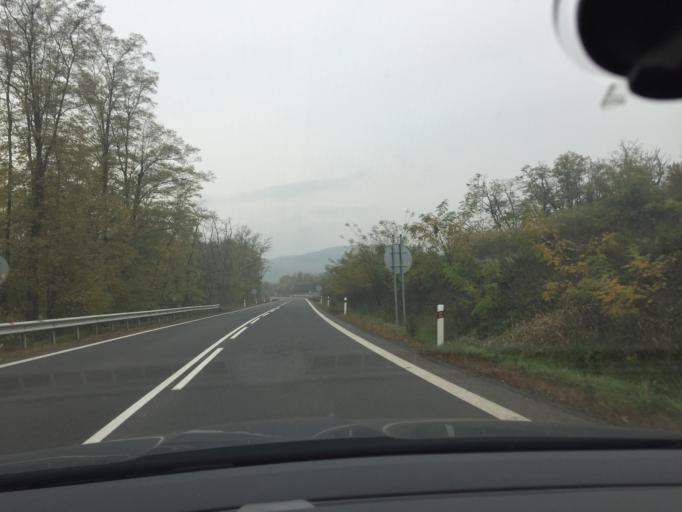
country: SK
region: Banskobystricky
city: Velky Krtis
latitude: 48.2229
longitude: 19.3998
